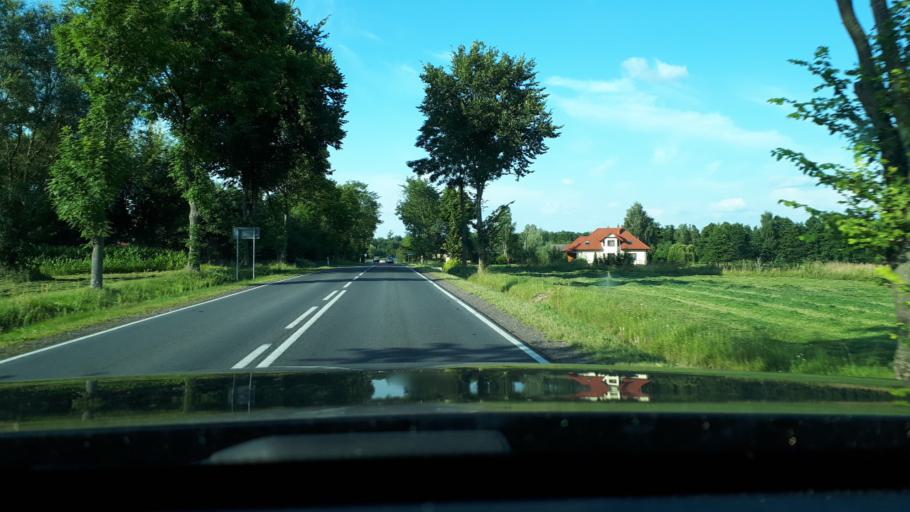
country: PL
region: Masovian Voivodeship
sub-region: Powiat plonski
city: Sochocin
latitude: 52.7044
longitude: 20.4894
